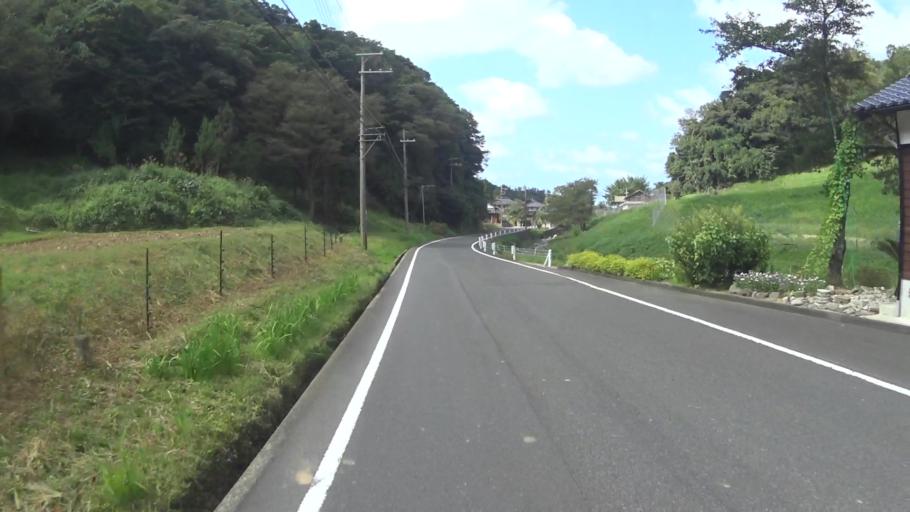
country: JP
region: Kyoto
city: Miyazu
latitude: 35.7448
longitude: 135.1802
